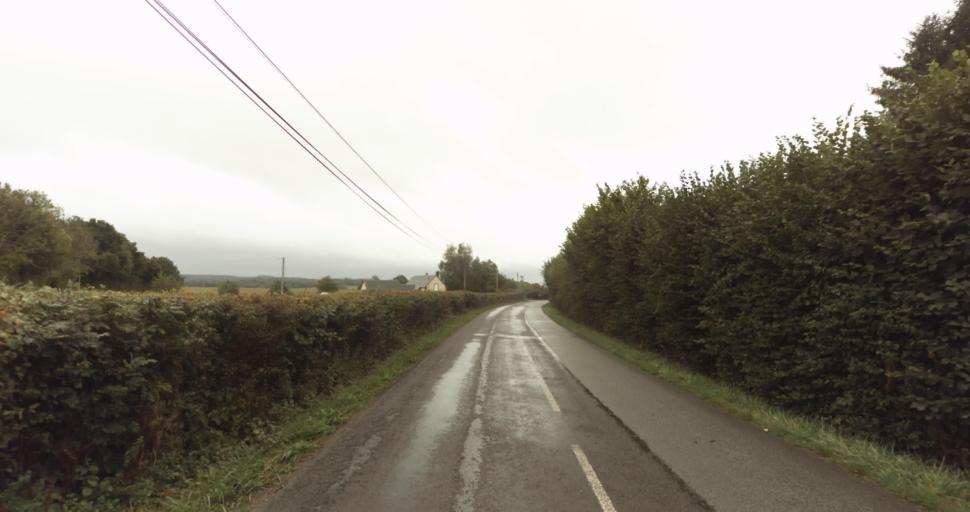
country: FR
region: Lower Normandy
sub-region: Departement de l'Orne
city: Sainte-Gauburge-Sainte-Colombe
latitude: 48.7322
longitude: 0.4364
